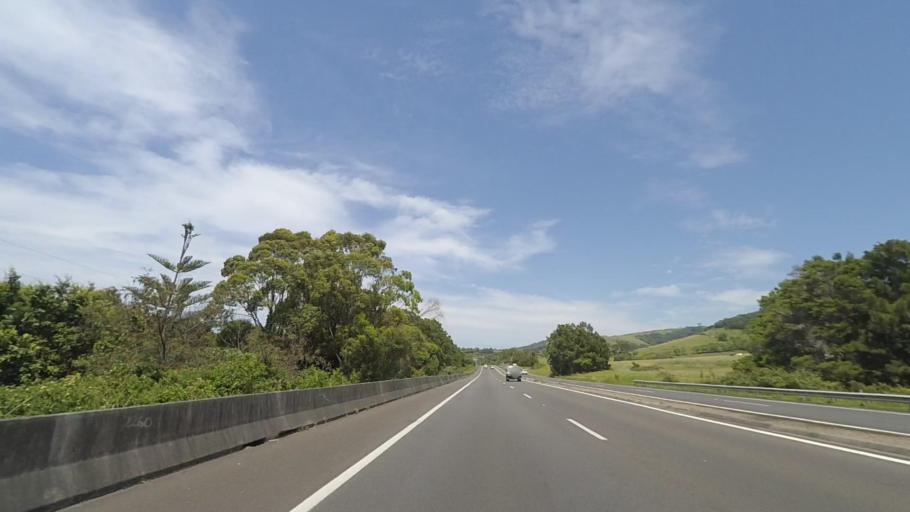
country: AU
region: New South Wales
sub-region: Kiama
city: Kiama
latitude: -34.6838
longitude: 150.8444
